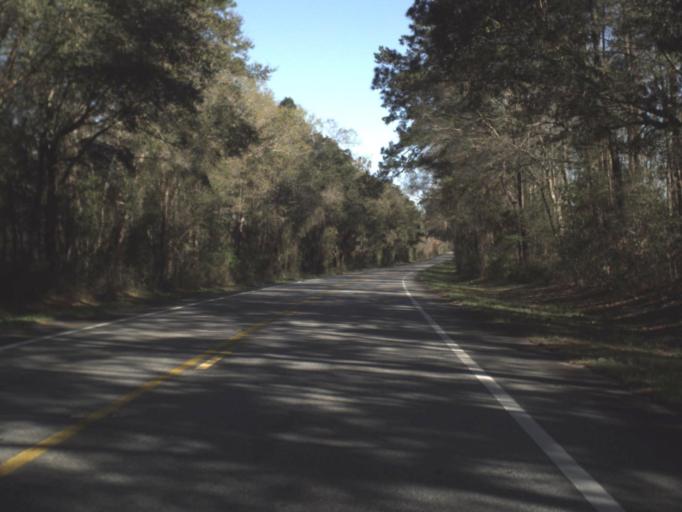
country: US
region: Georgia
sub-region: Brooks County
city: Quitman
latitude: 30.5860
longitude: -83.6389
